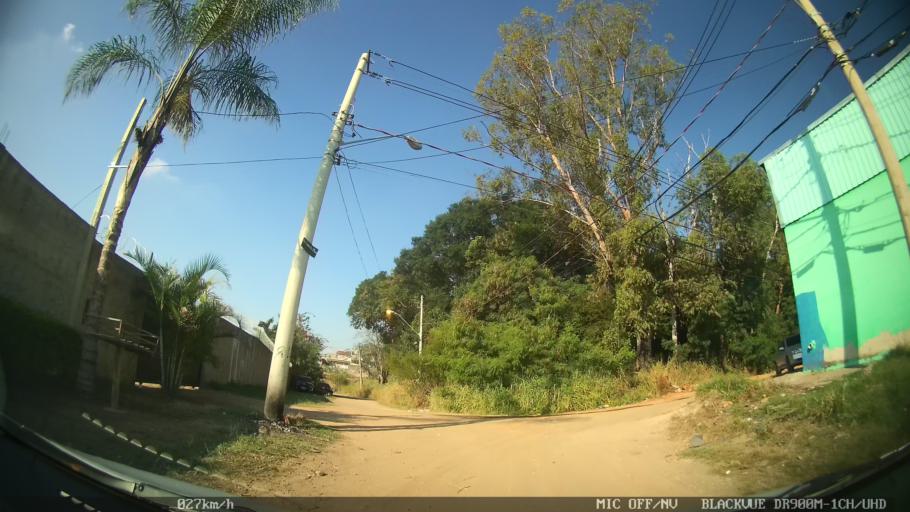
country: BR
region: Sao Paulo
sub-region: Campinas
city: Campinas
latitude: -22.9877
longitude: -47.1439
